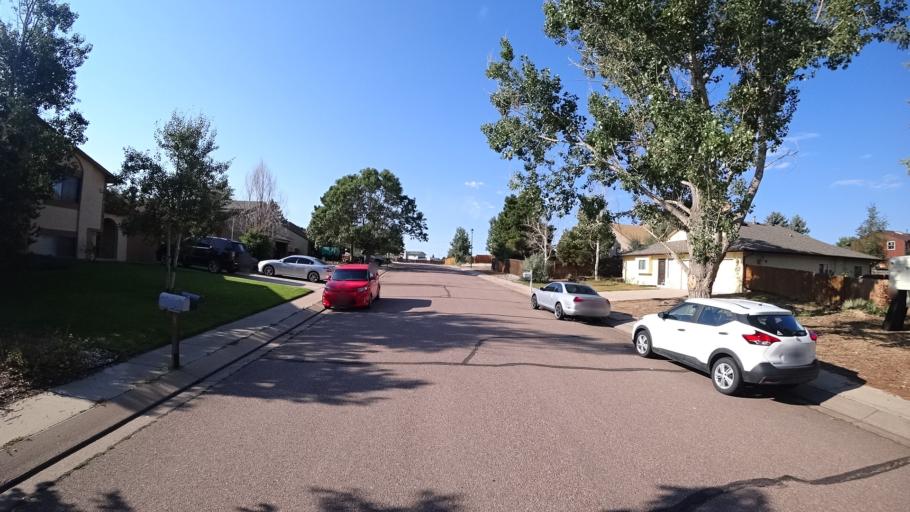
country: US
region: Colorado
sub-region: El Paso County
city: Black Forest
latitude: 38.9429
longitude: -104.7661
